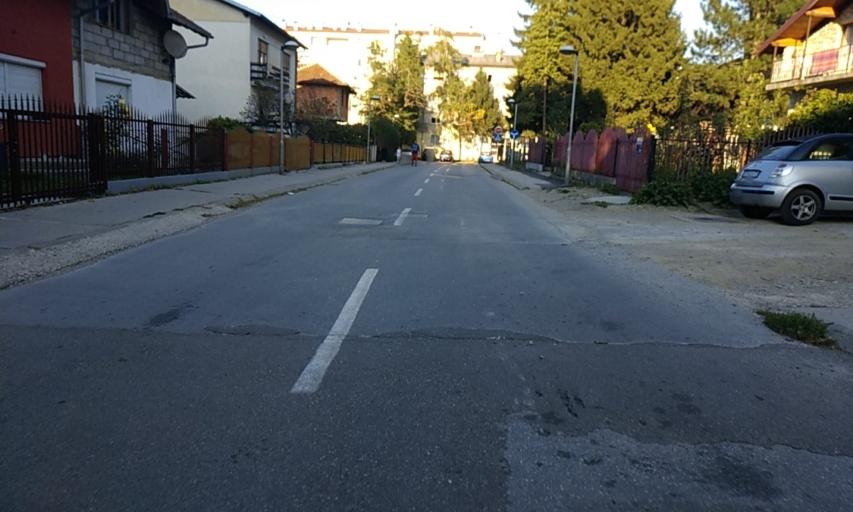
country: BA
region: Republika Srpska
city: Mejdan - Obilicevo
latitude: 44.7583
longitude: 17.1892
